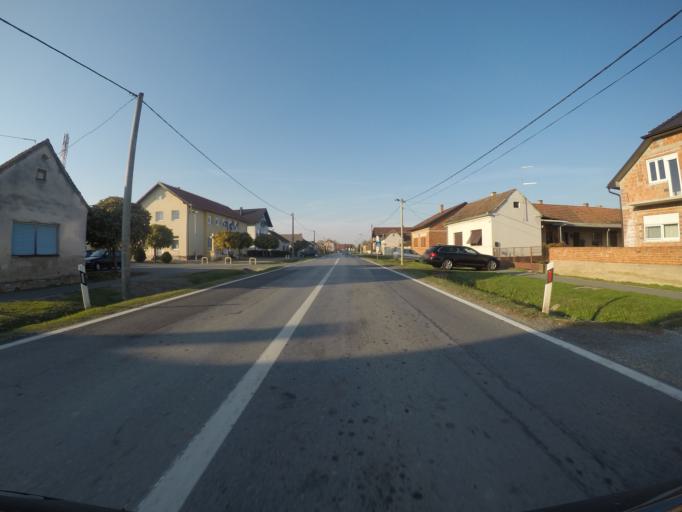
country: HU
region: Somogy
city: Barcs
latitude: 45.9060
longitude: 17.4417
